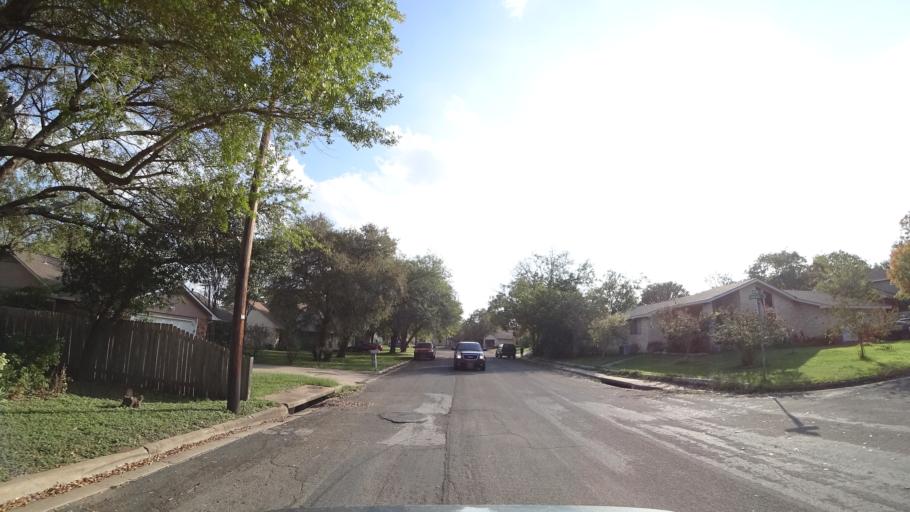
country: US
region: Texas
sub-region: Williamson County
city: Round Rock
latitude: 30.4942
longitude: -97.6675
